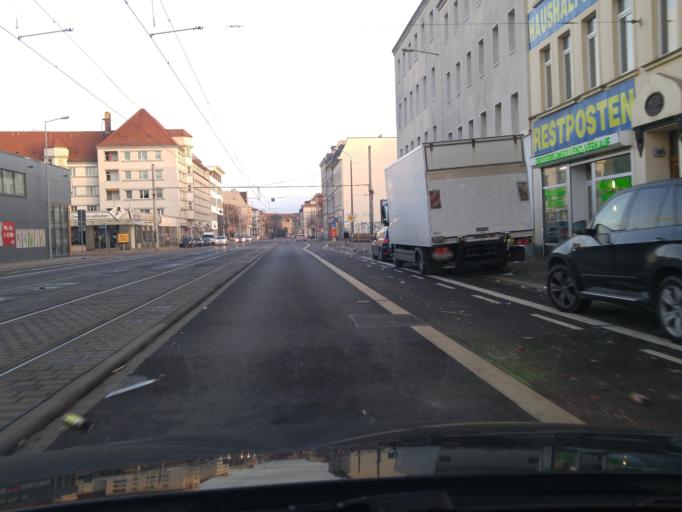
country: DE
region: Saxony
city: Leipzig
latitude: 51.3619
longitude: 12.3678
